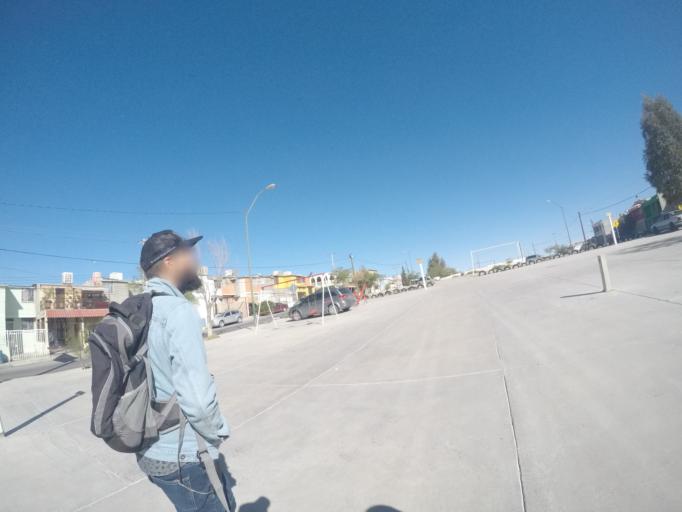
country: US
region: Texas
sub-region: El Paso County
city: Socorro
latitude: 31.6667
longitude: -106.4015
